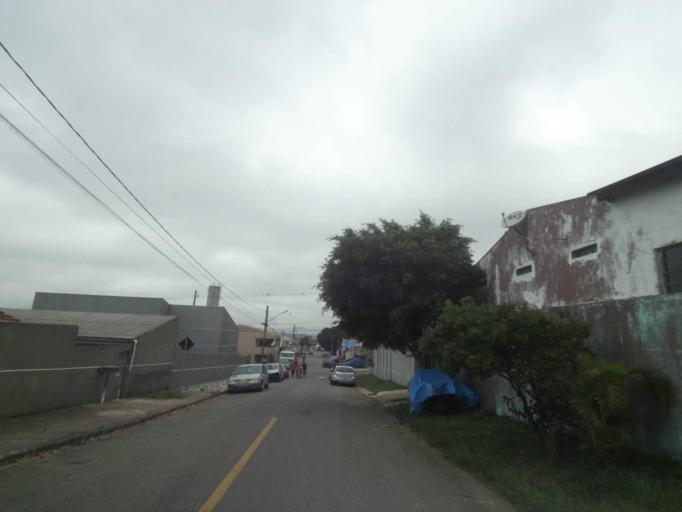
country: BR
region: Parana
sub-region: Curitiba
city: Curitiba
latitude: -25.4948
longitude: -49.3518
